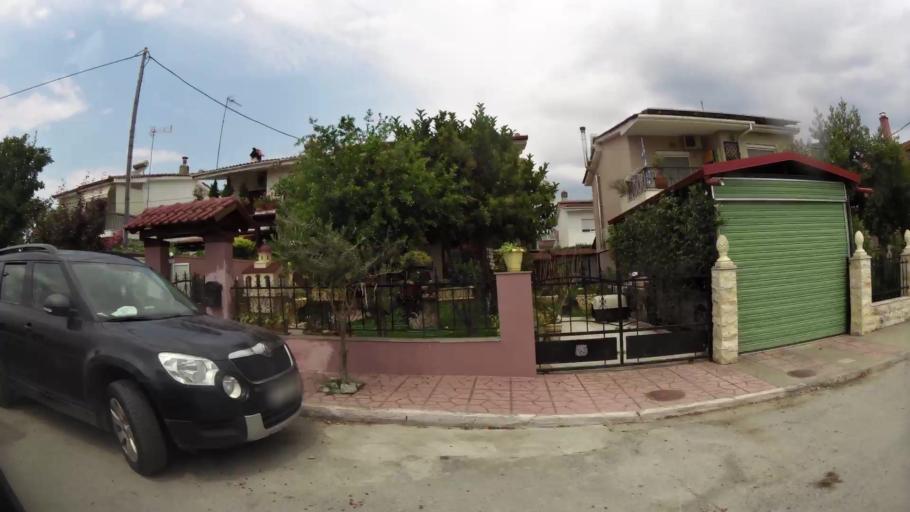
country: GR
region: Central Macedonia
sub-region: Nomos Pierias
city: Kallithea
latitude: 40.2732
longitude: 22.5718
